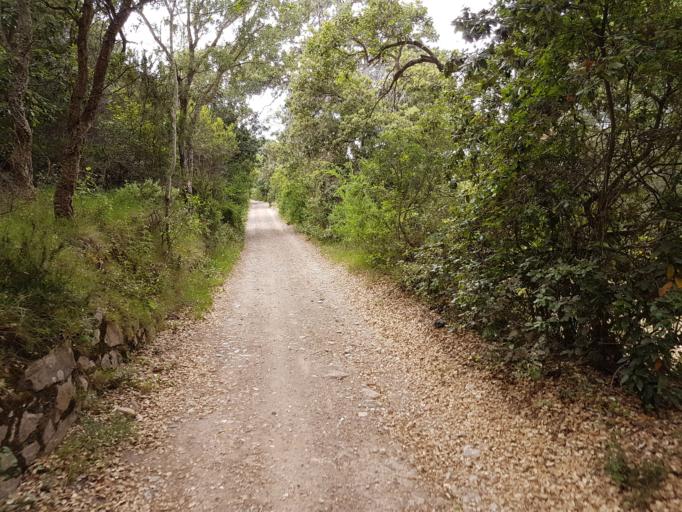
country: IT
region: Tuscany
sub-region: Provincia di Livorno
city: Portoferraio
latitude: 42.7847
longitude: 10.3506
